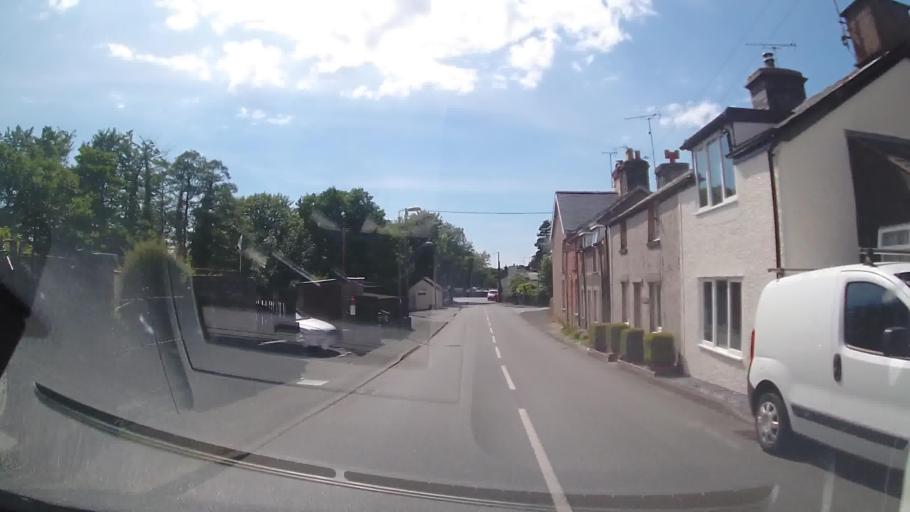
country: GB
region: Wales
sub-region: Gwynedd
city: Tywyn
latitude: 52.6100
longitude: -4.0539
